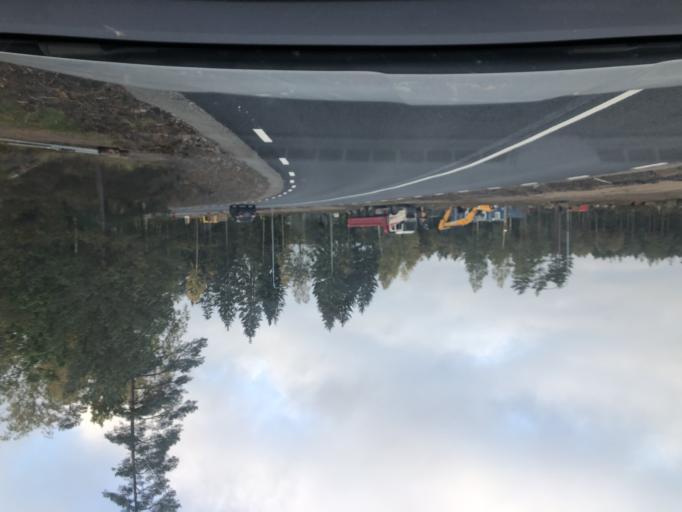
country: SE
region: Vaestra Goetaland
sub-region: Trollhattan
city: Trollhattan
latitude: 58.3146
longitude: 12.2709
